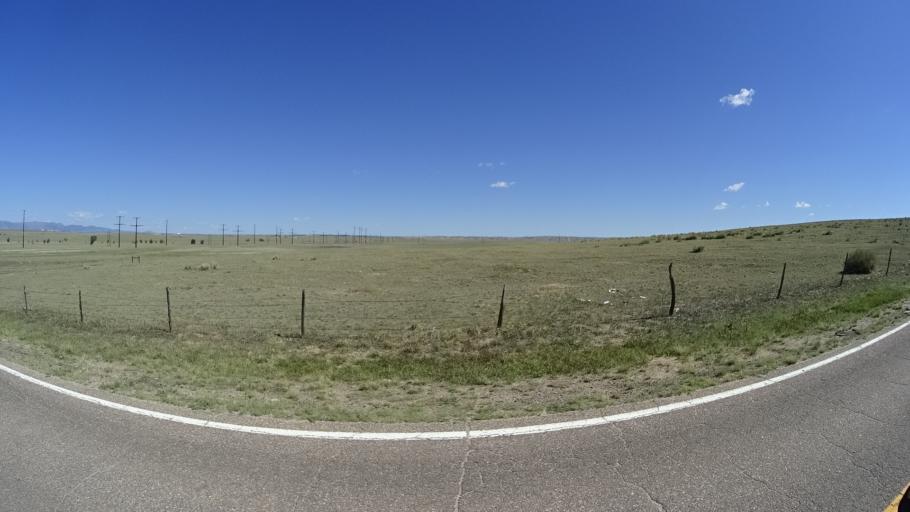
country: US
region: Colorado
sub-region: El Paso County
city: Security-Widefield
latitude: 38.7809
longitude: -104.6240
